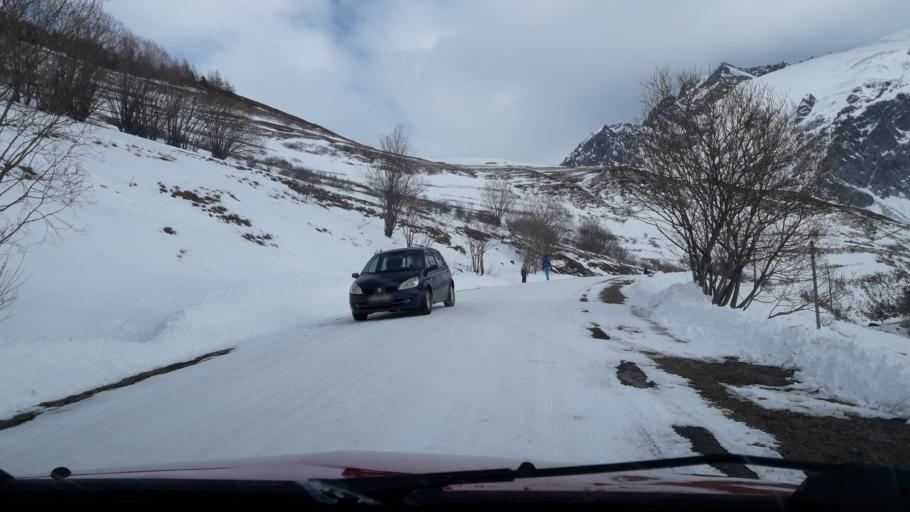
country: FR
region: Rhone-Alpes
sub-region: Departement de l'Isere
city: Mont-de-Lans
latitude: 45.0540
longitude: 6.2869
